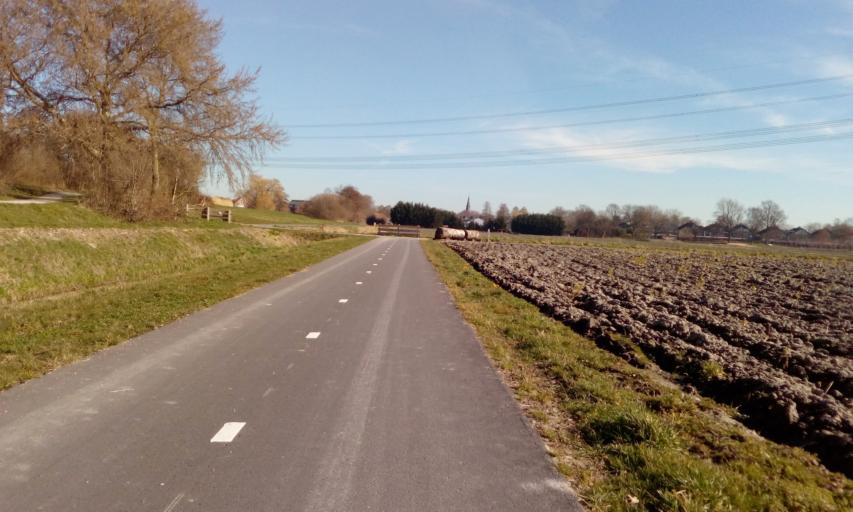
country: NL
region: South Holland
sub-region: Gemeente Lansingerland
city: Bleiswijk
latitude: 52.0092
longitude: 4.5709
